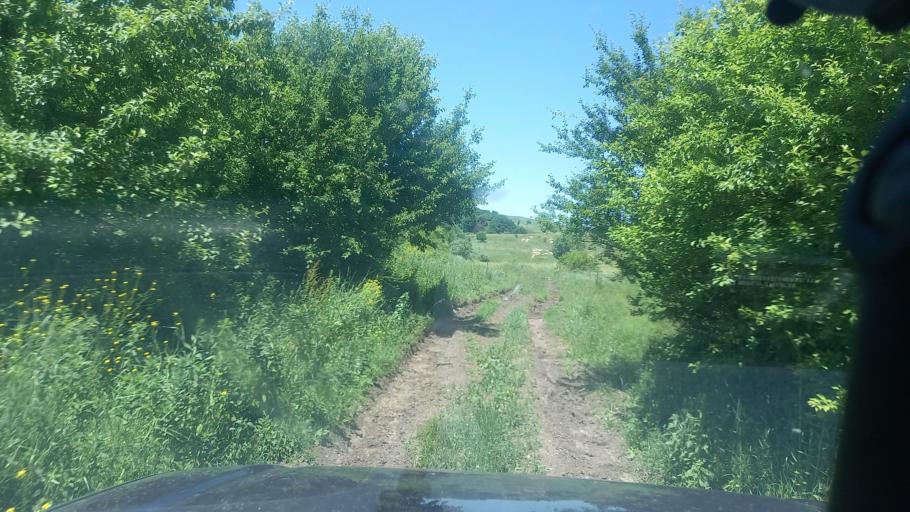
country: RU
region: Karachayevo-Cherkesiya
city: Pregradnaya
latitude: 44.1092
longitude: 41.1257
